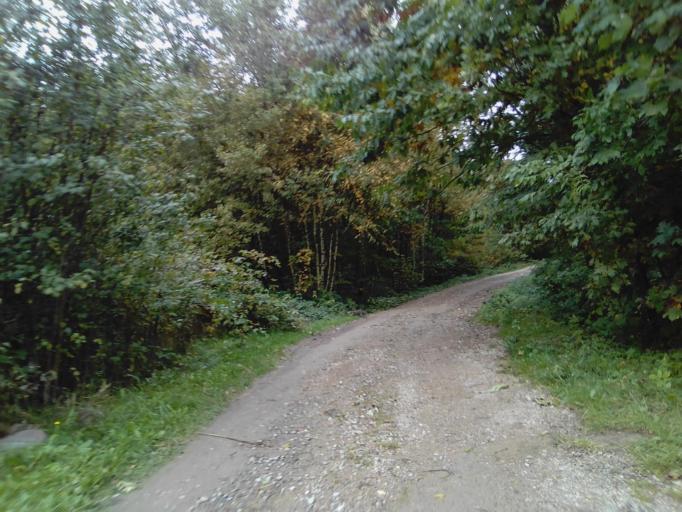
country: PL
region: Subcarpathian Voivodeship
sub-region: Powiat strzyzowski
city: Gwoznica Gorna
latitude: 49.8374
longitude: 22.0201
